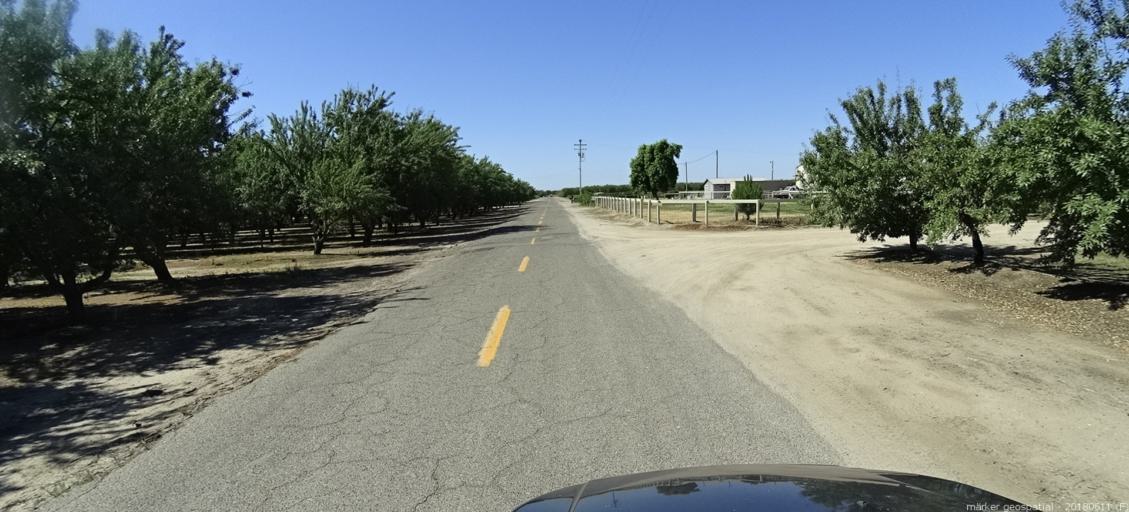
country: US
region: California
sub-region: Madera County
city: Madera
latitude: 36.9578
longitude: -120.1750
